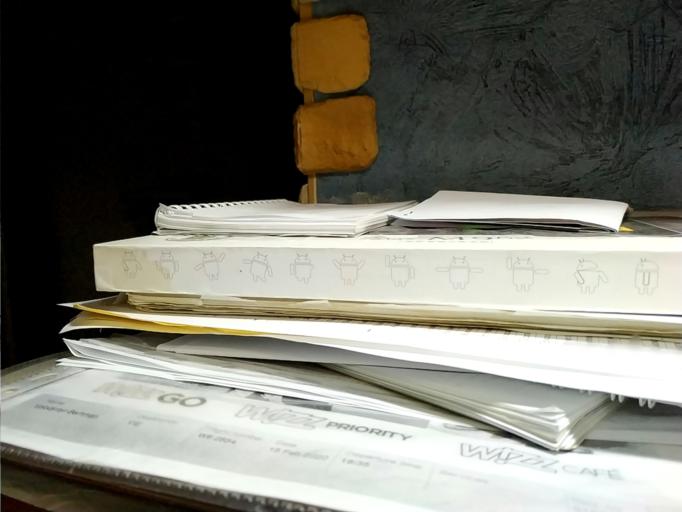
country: RU
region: Arkhangelskaya
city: Onega
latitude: 63.2160
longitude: 38.3129
